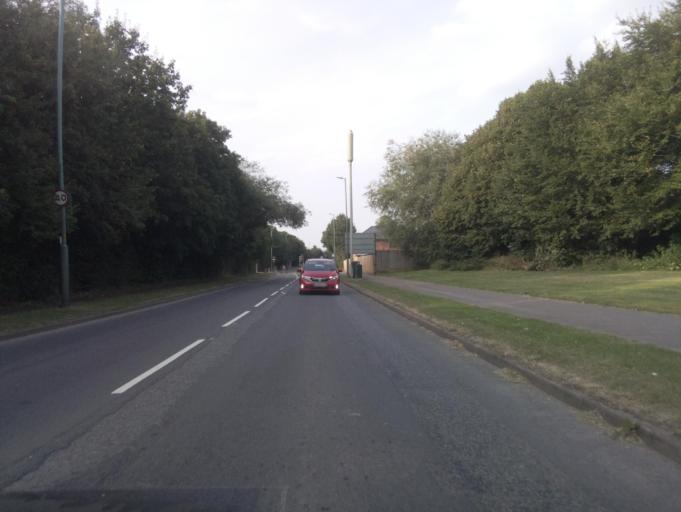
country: GB
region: England
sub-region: Gloucestershire
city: Gotherington
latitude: 51.9464
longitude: -2.0725
